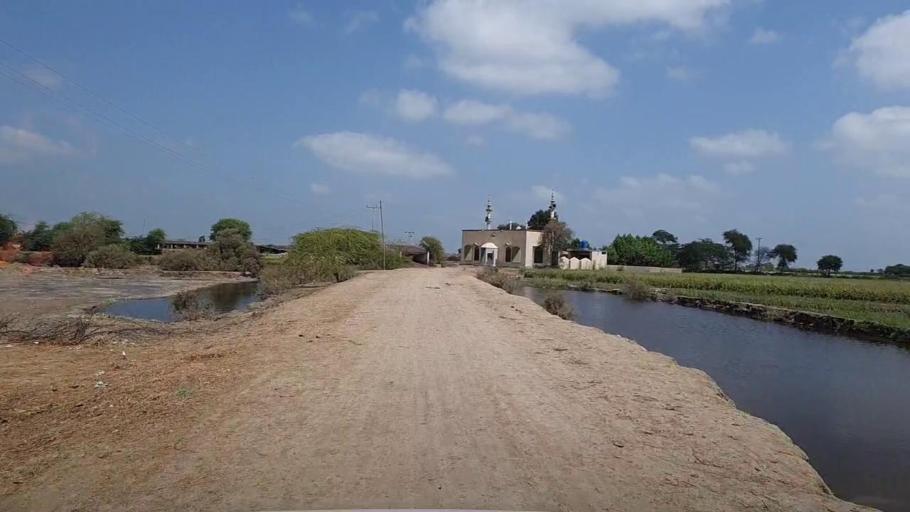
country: PK
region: Sindh
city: Kario
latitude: 24.6804
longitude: 68.5473
